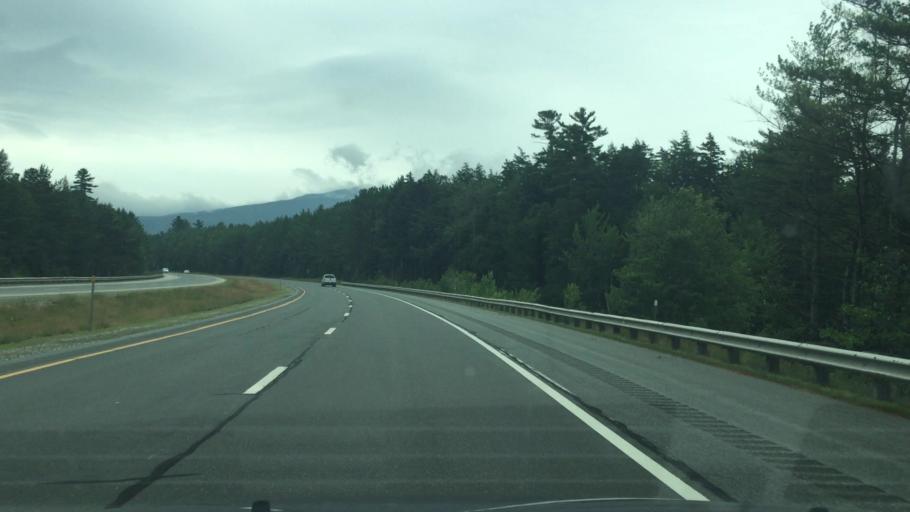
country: US
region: New Hampshire
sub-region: Grafton County
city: Deerfield
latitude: 44.2084
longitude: -71.7204
